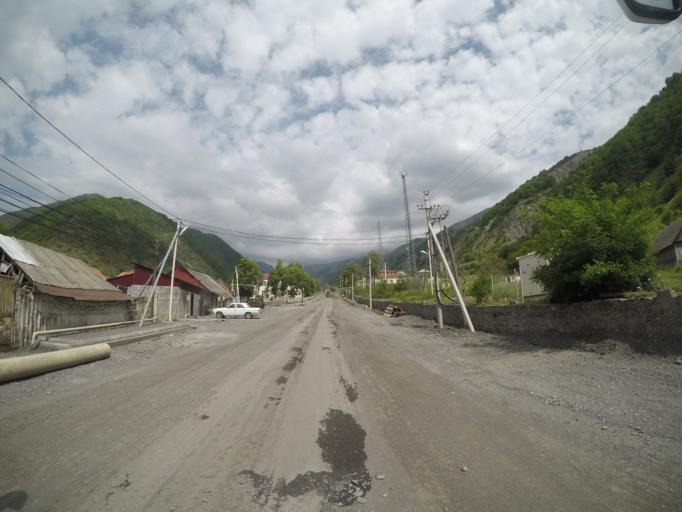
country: AZ
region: Qakh Rayon
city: Qaxbas
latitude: 41.4681
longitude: 47.0556
